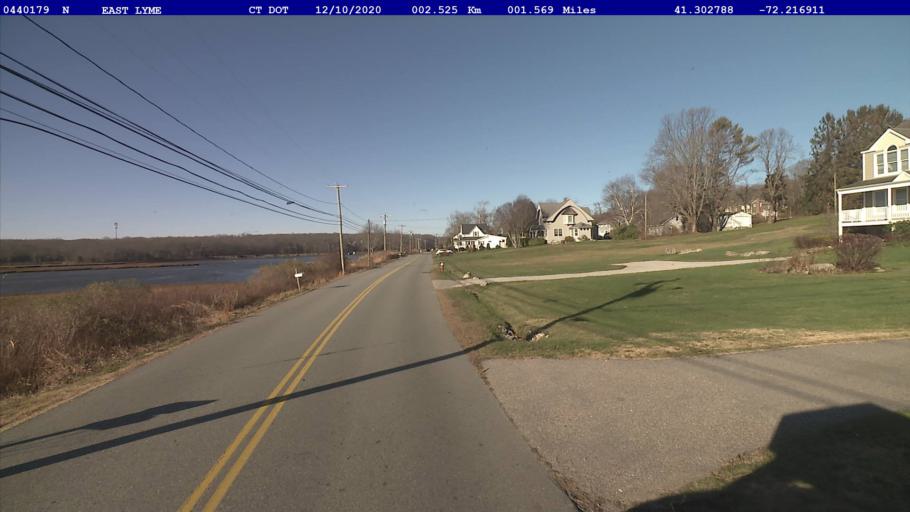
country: US
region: Connecticut
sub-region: New London County
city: Niantic
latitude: 41.3028
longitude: -72.2169
